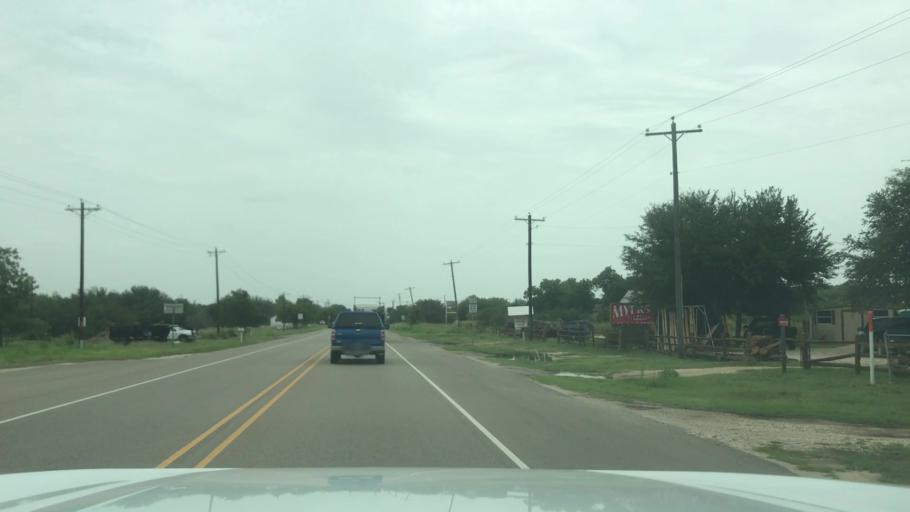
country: US
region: Texas
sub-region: Bosque County
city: Meridian
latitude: 31.9186
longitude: -97.6710
